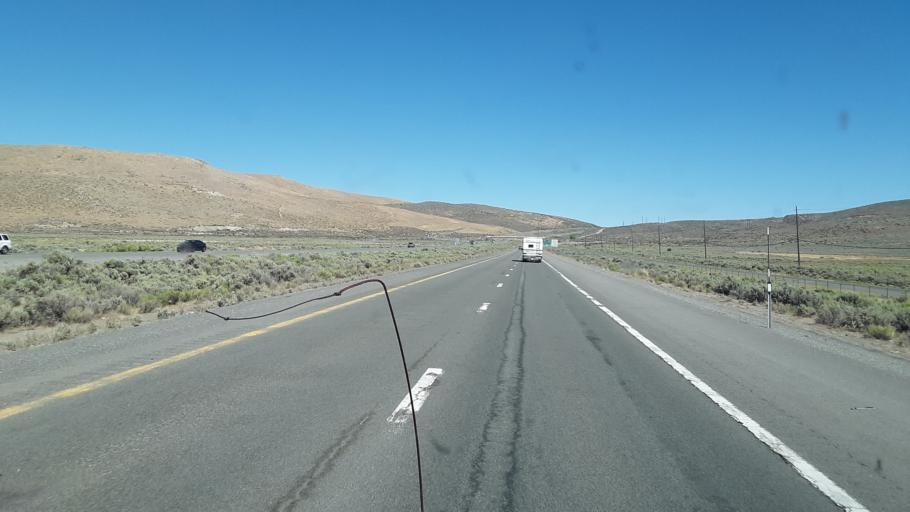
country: US
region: Nevada
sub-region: Washoe County
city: Cold Springs
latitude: 39.6482
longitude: -119.9713
